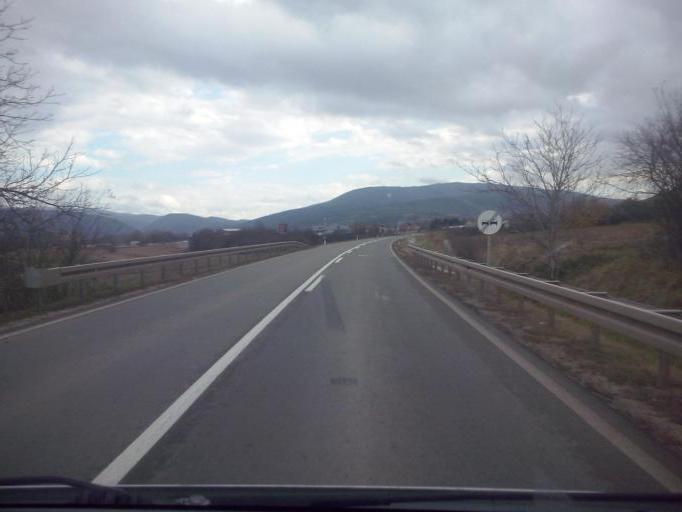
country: RS
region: Central Serbia
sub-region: Pomoravski Okrug
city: Paracin
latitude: 43.8578
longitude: 21.5493
